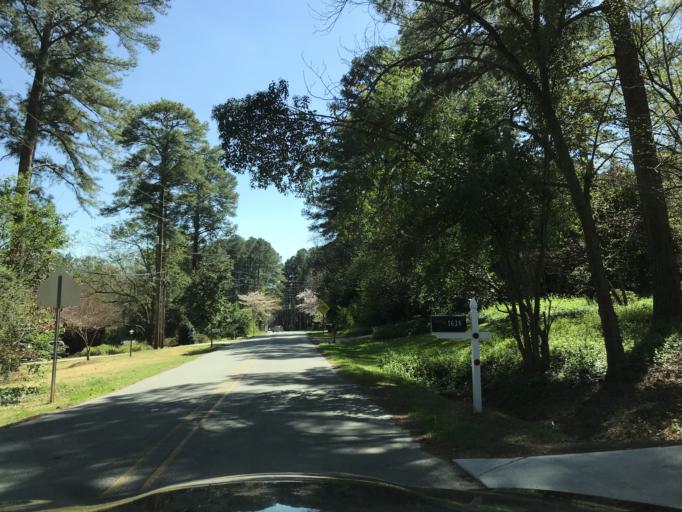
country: US
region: North Carolina
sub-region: Wake County
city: West Raleigh
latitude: 35.7682
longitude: -78.7053
